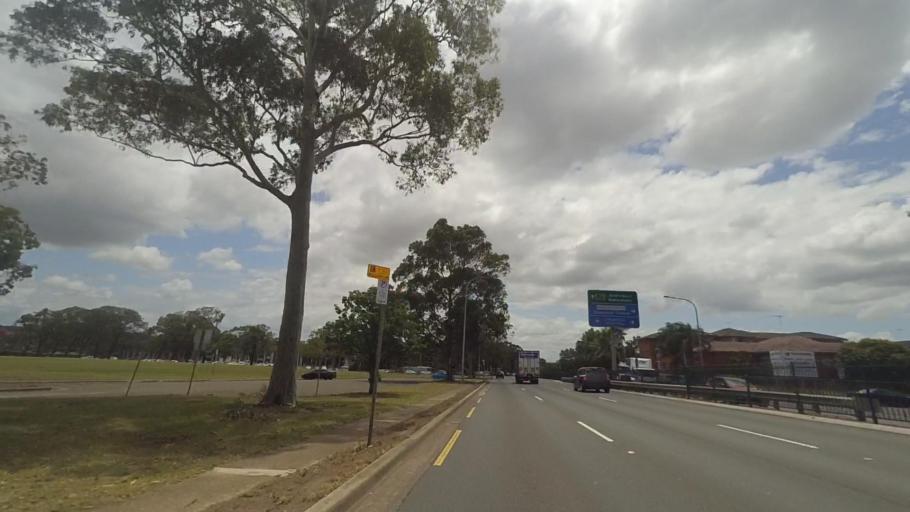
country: AU
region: New South Wales
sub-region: Fairfield
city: Cabramatta West
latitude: -33.9258
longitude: 150.9179
